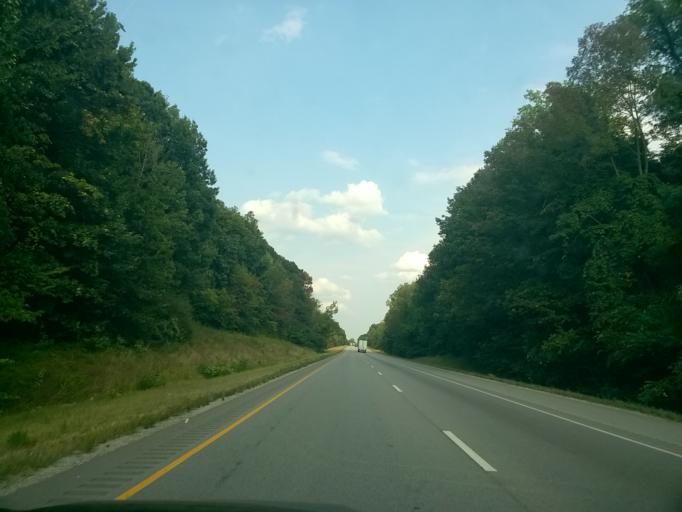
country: US
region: Indiana
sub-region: Vigo County
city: Seelyville
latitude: 39.4436
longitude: -87.2652
